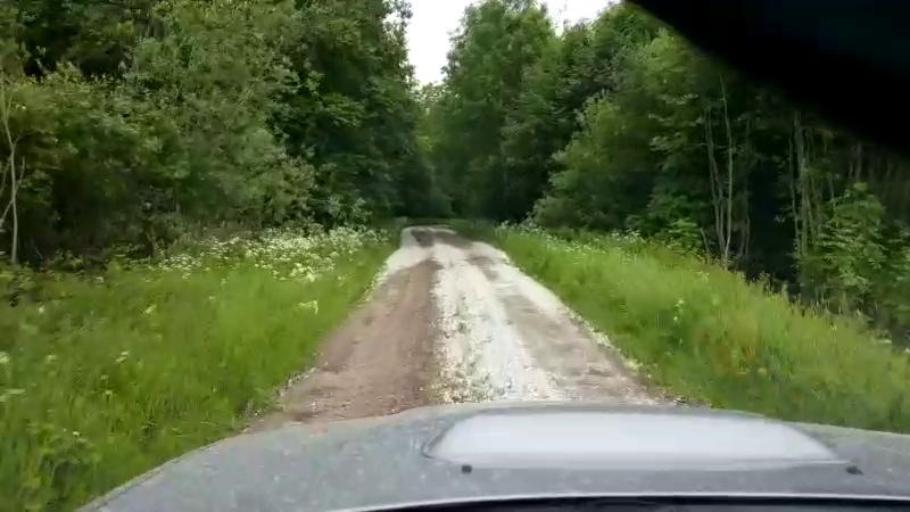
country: EE
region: Paernumaa
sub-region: Tootsi vald
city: Tootsi
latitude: 58.5948
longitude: 24.6628
